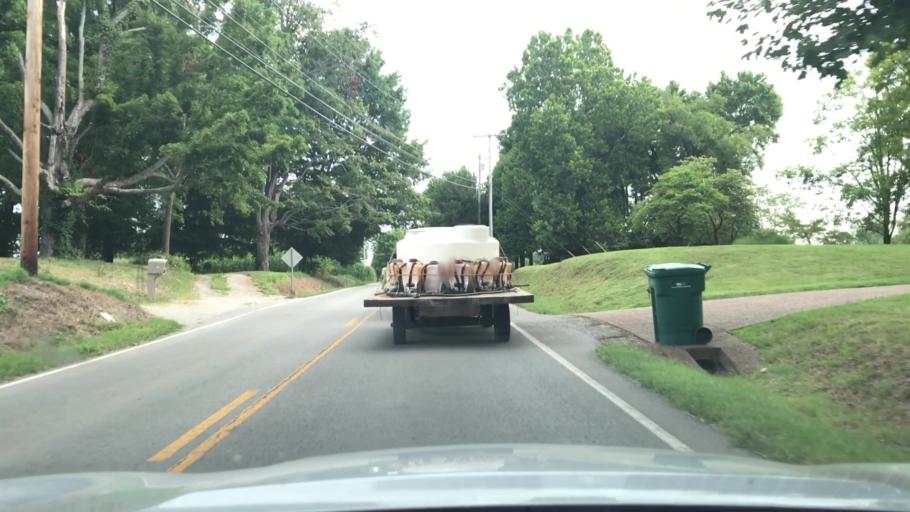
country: US
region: Kentucky
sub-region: Todd County
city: Elkton
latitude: 36.8148
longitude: -87.1526
